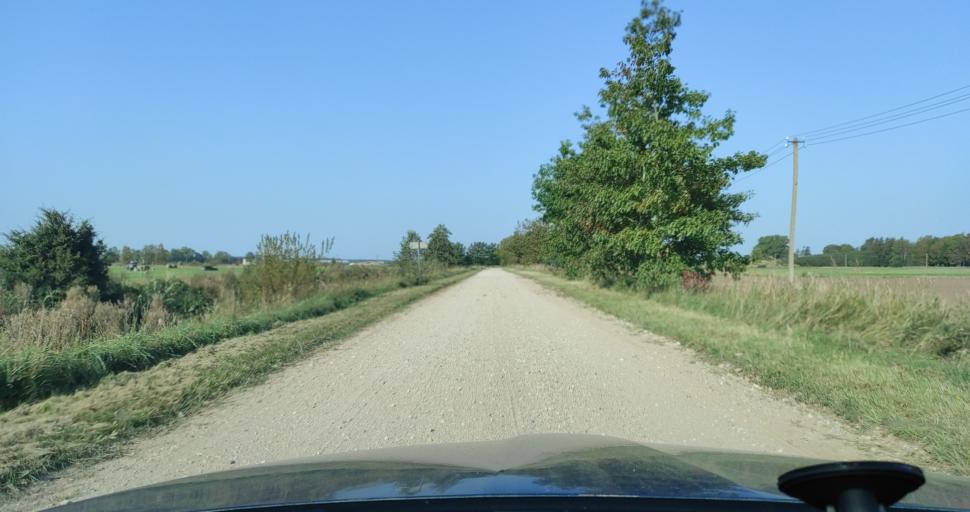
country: LV
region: Ventspils Rajons
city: Piltene
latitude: 57.2314
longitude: 21.6128
